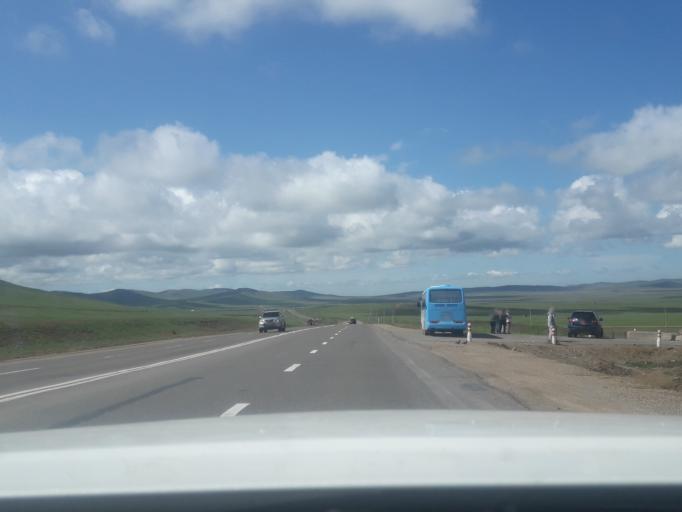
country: MN
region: Central Aimak
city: Altanbulag
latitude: 47.9007
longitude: 106.5026
